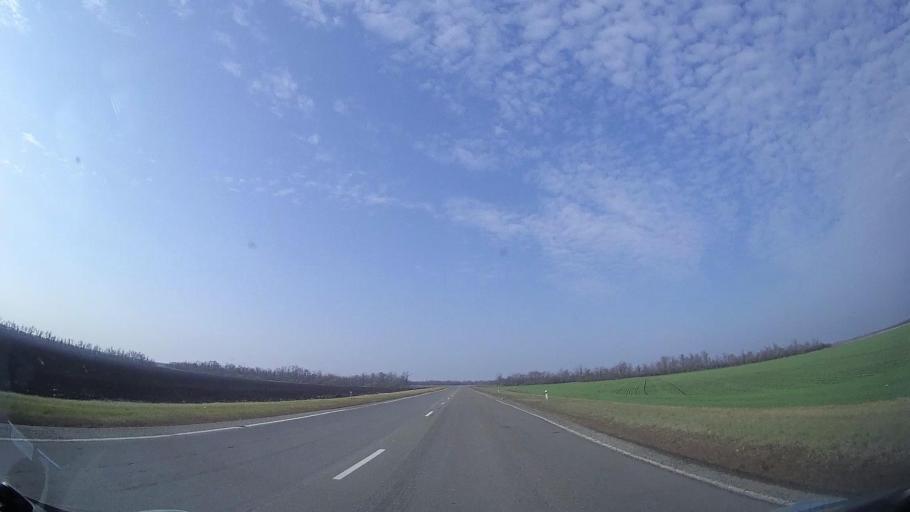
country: RU
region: Rostov
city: Tselina
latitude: 46.5135
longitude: 41.0323
